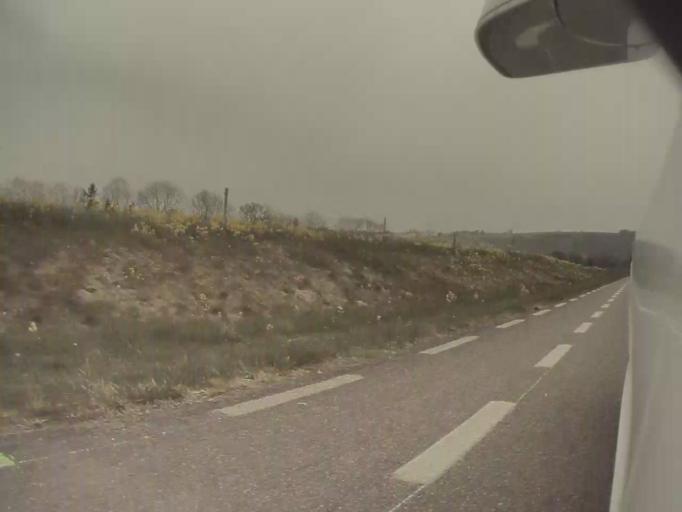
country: BE
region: Wallonia
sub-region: Province du Luxembourg
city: Durbuy
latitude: 50.3924
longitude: 5.4916
